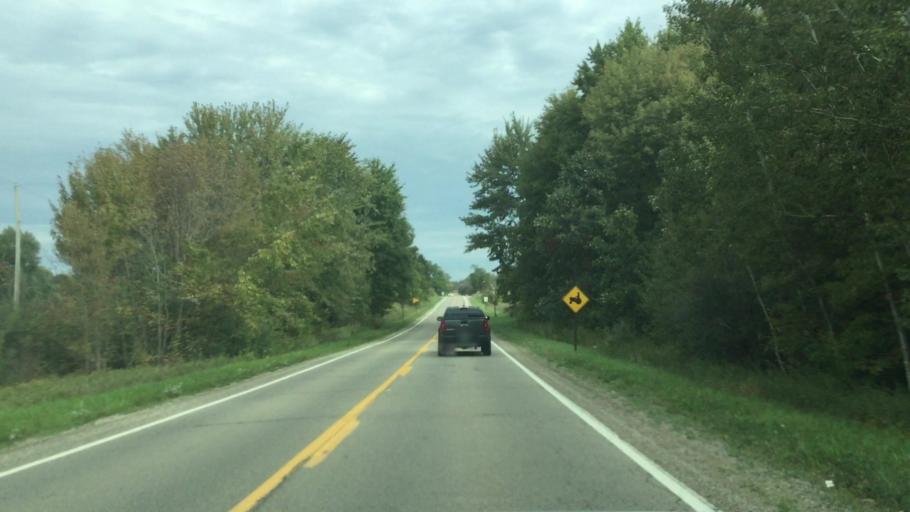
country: US
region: Michigan
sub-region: Genesee County
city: Argentine
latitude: 42.6968
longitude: -83.8793
